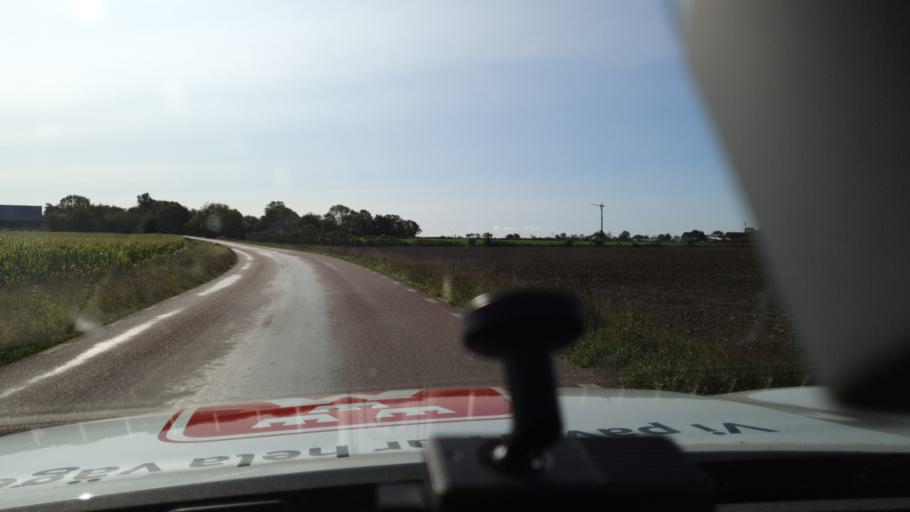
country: SE
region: Gotland
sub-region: Gotland
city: Hemse
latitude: 57.1535
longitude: 18.2815
